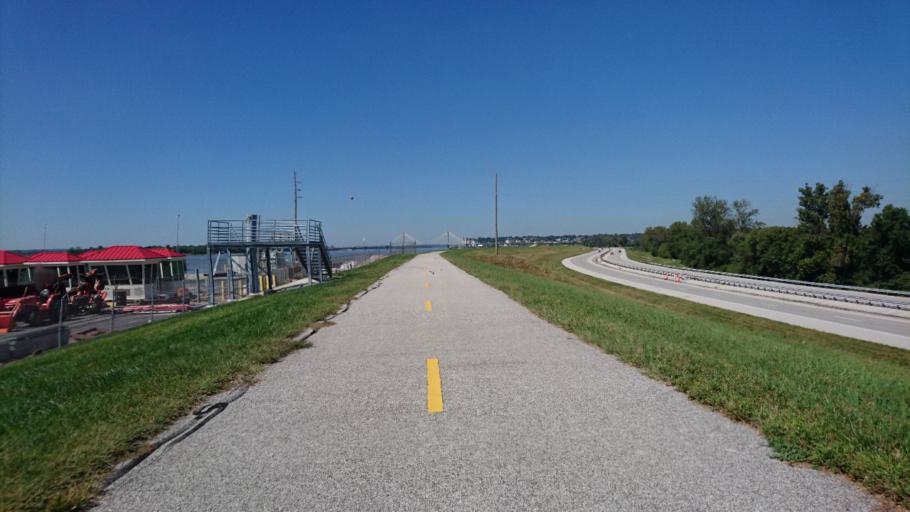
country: US
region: Illinois
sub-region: Madison County
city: Alton
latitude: 38.8720
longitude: -90.1517
